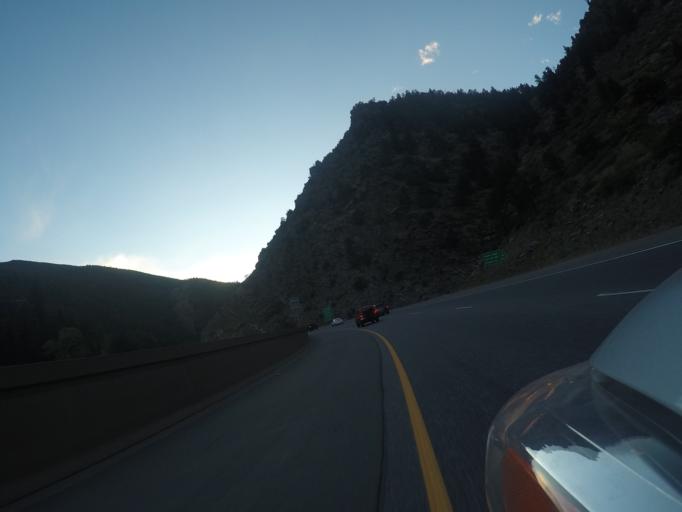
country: US
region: Colorado
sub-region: Clear Creek County
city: Idaho Springs
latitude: 39.7445
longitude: -105.4473
